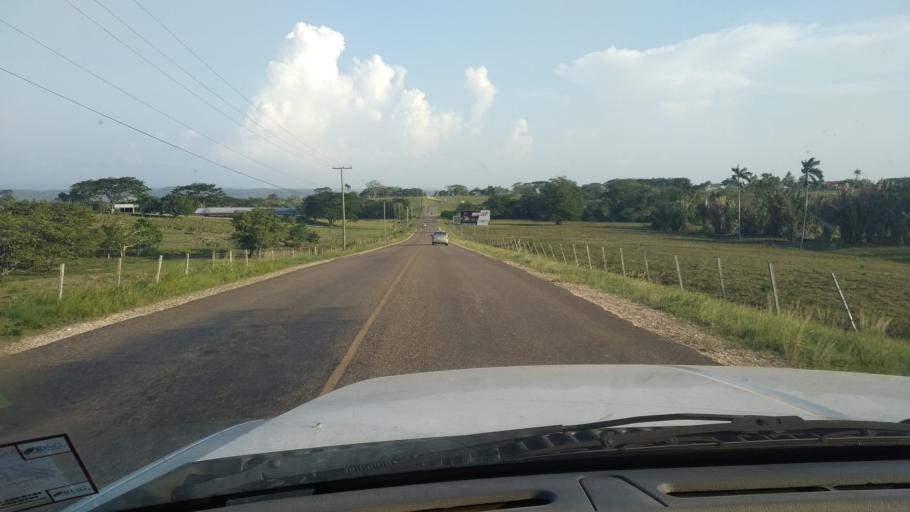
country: BZ
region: Cayo
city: San Ignacio
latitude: 17.2520
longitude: -88.9873
